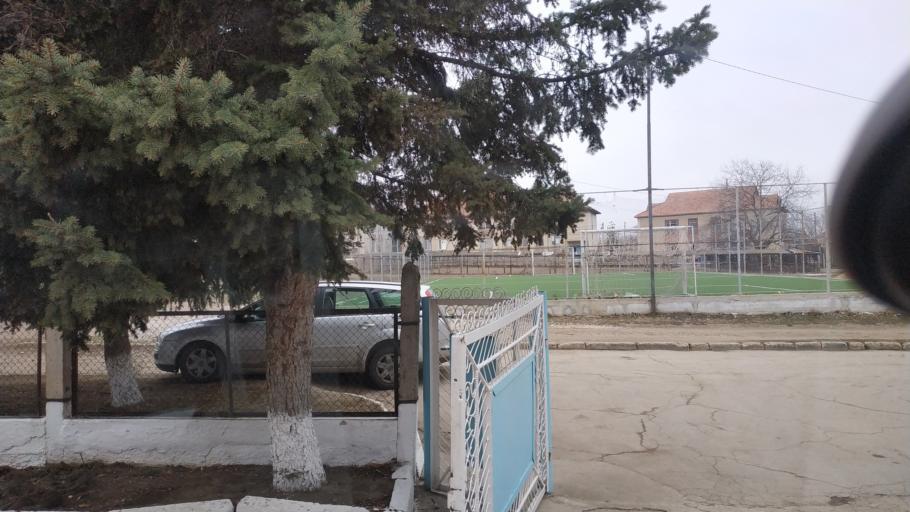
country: MD
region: Telenesti
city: Cocieri
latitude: 47.3793
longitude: 29.1204
